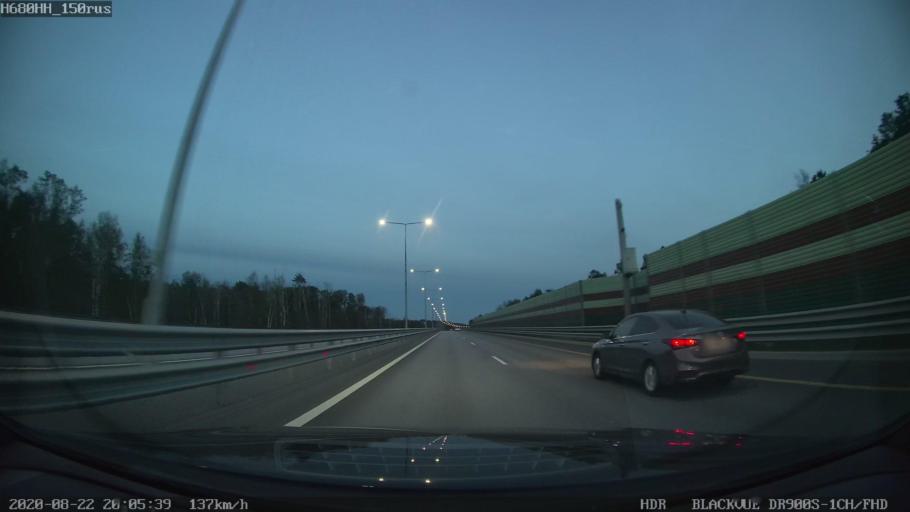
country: RU
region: Tverskaya
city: Radchenko
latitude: 56.6282
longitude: 36.4282
